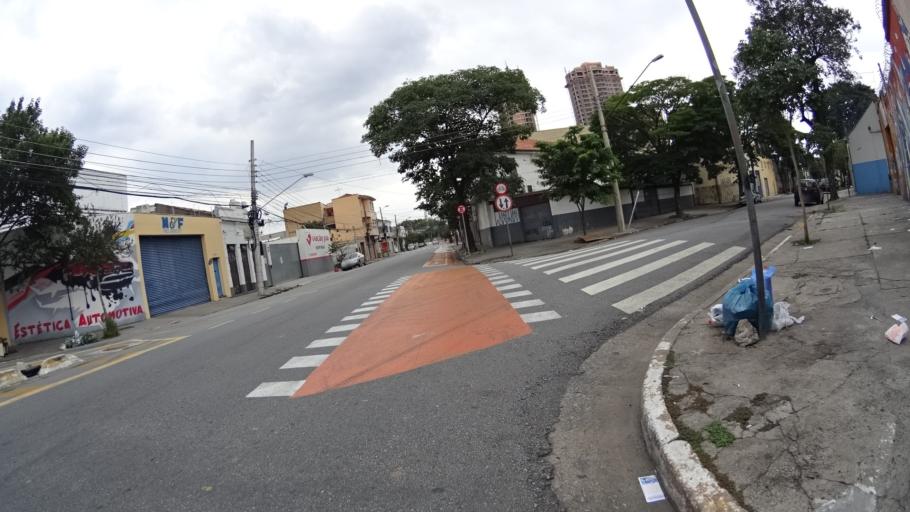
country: BR
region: Sao Paulo
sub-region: Sao Paulo
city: Sao Paulo
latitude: -23.5257
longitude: -46.6532
